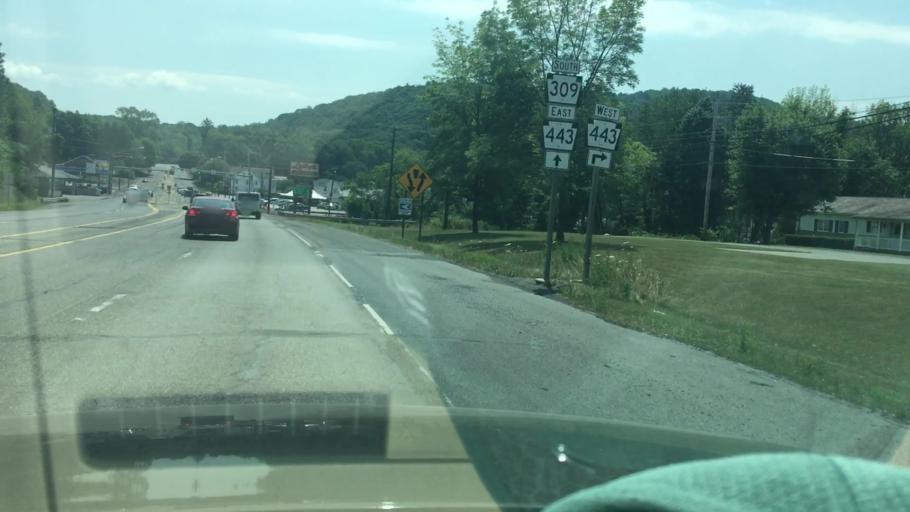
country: US
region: Pennsylvania
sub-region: Schuylkill County
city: Tamaqua
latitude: 40.7595
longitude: -75.9473
